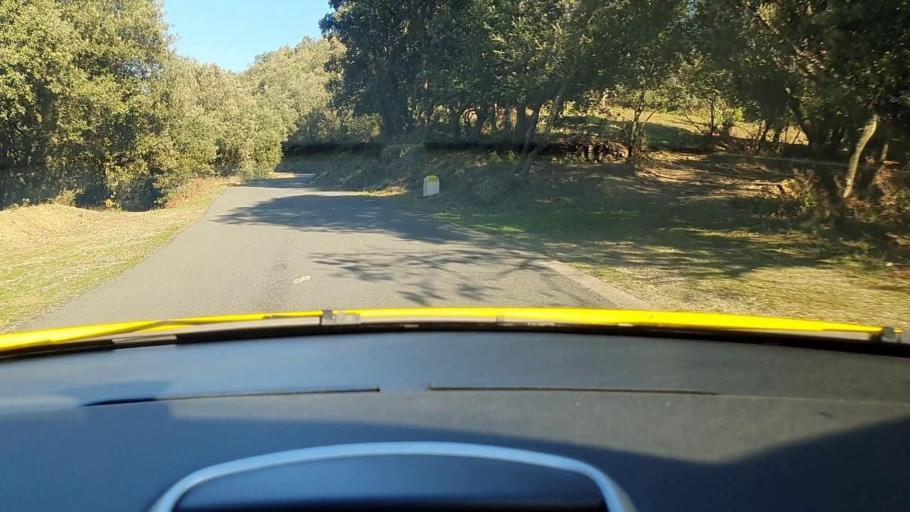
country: FR
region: Languedoc-Roussillon
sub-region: Departement du Gard
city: Sumene
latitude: 44.0200
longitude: 3.7455
